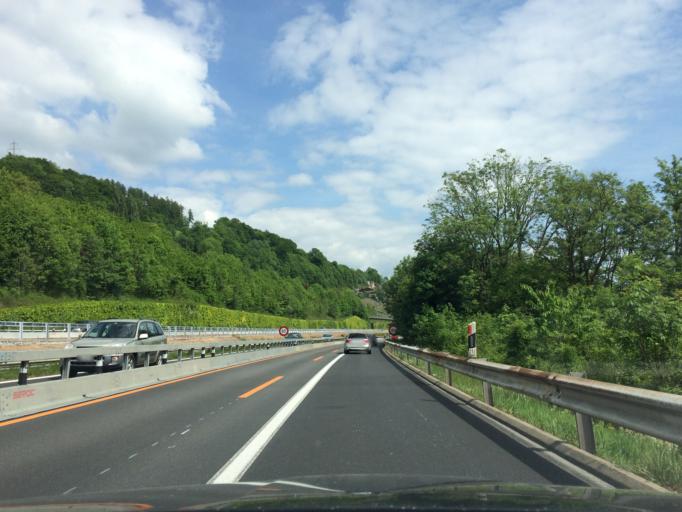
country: CH
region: Vaud
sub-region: Lavaux-Oron District
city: Chexbres
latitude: 46.4815
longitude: 6.7886
